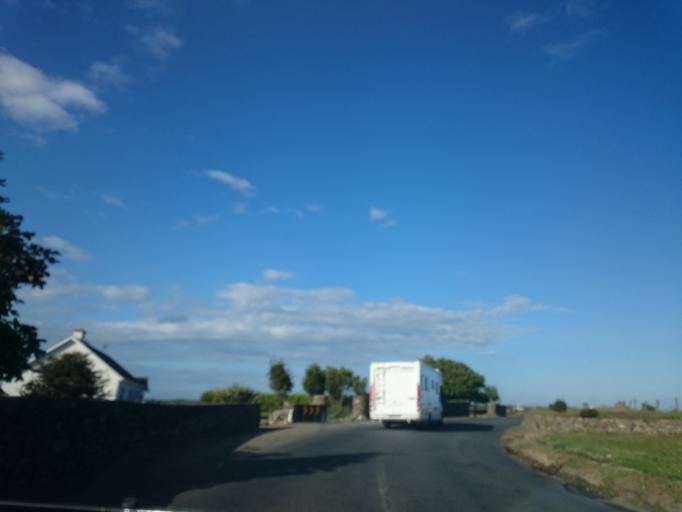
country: IE
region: Leinster
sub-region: Loch Garman
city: Loch Garman
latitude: 52.1874
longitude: -6.5674
